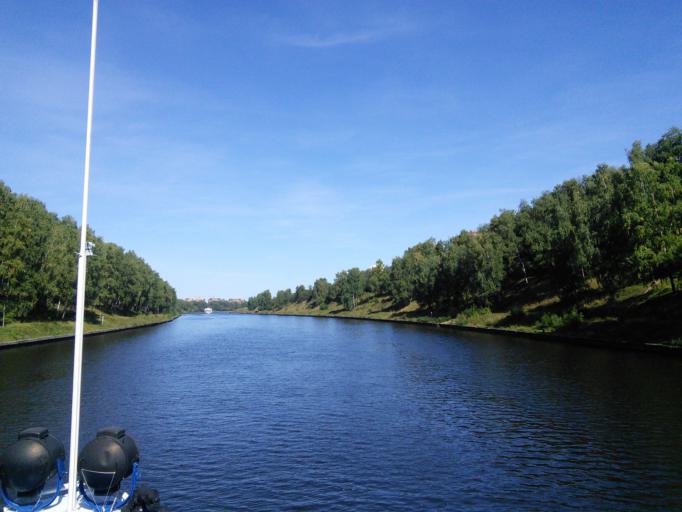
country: RU
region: Moskovskaya
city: Dolgoprudnyy
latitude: 55.9322
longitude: 37.4884
